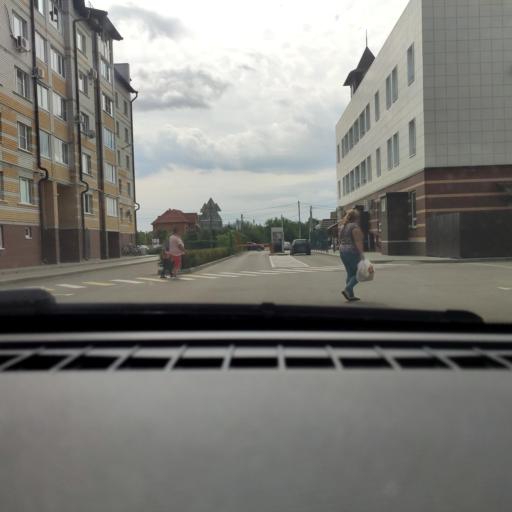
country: RU
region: Voronezj
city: Novaya Usman'
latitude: 51.6504
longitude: 39.3321
